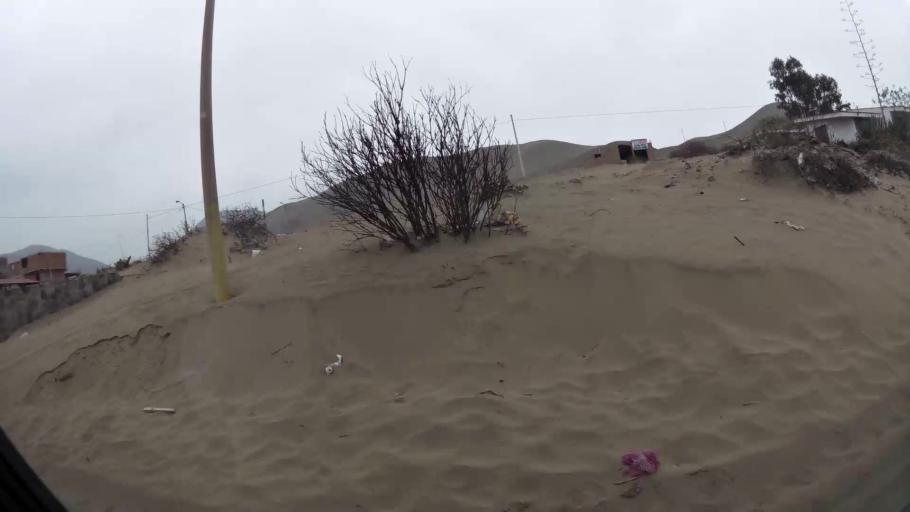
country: PE
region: Lima
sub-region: Lima
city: Santa Rosa
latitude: -11.8036
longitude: -77.1741
